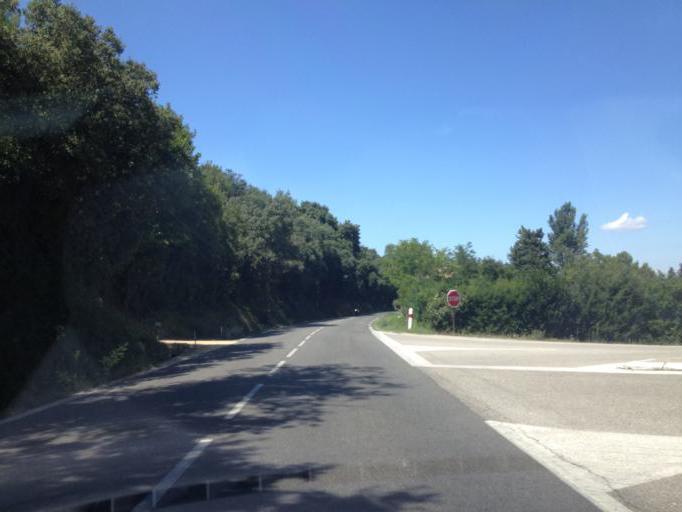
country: FR
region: Languedoc-Roussillon
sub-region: Departement du Gard
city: Sauveterre
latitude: 44.0142
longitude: 4.7975
